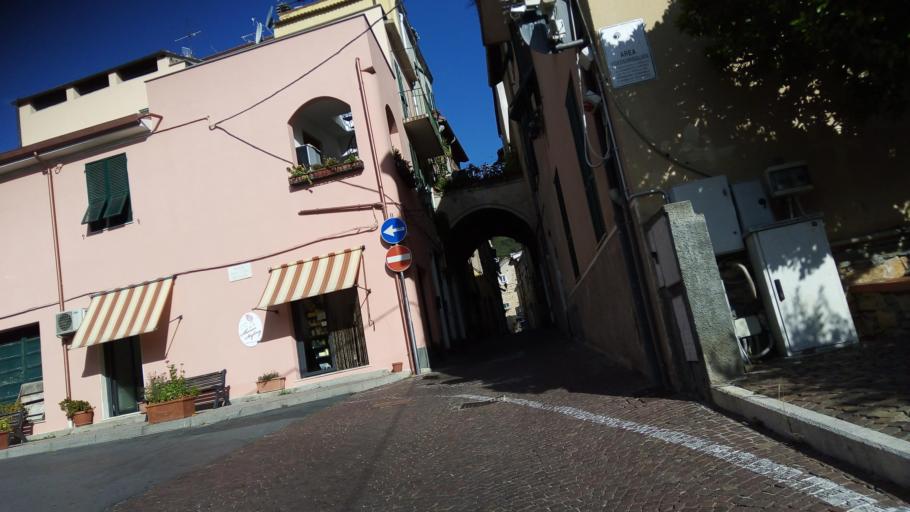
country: IT
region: Liguria
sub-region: Provincia di Savona
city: Toirano
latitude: 44.1270
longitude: 8.2072
